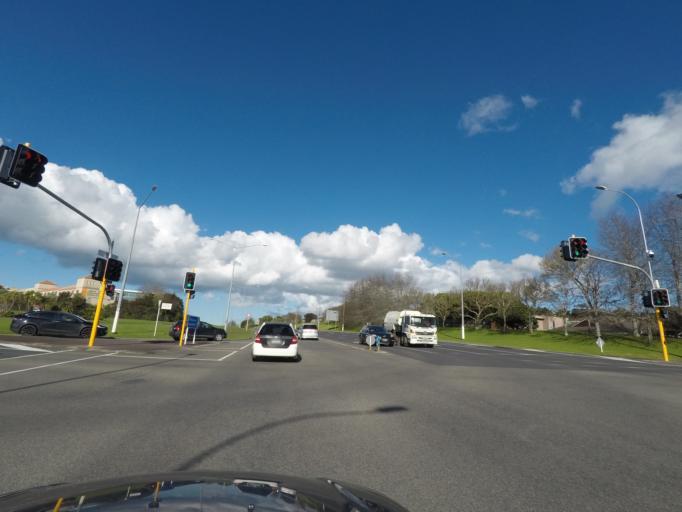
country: NZ
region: Auckland
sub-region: Auckland
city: Rothesay Bay
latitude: -36.7335
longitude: 174.7079
